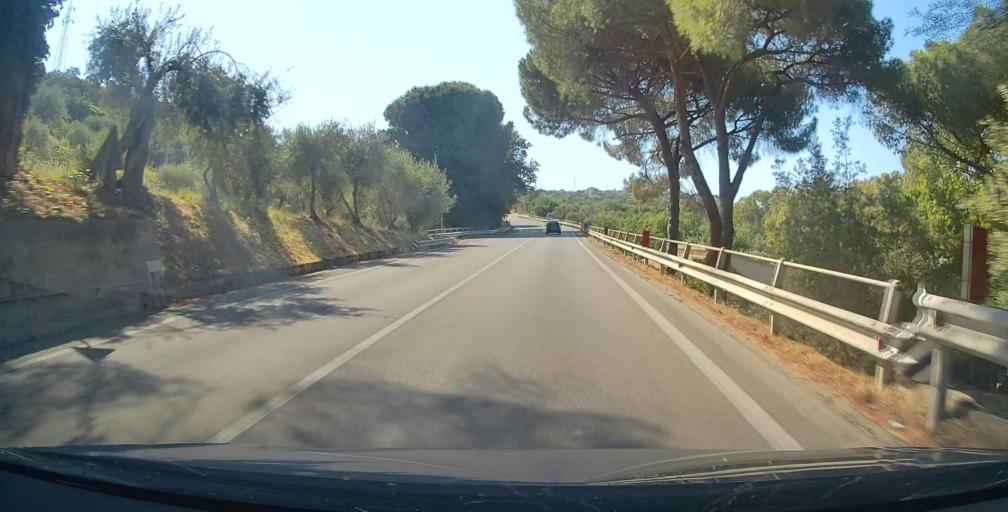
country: IT
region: Sicily
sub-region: Messina
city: Capo d'Orlando
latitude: 38.1531
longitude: 14.7616
